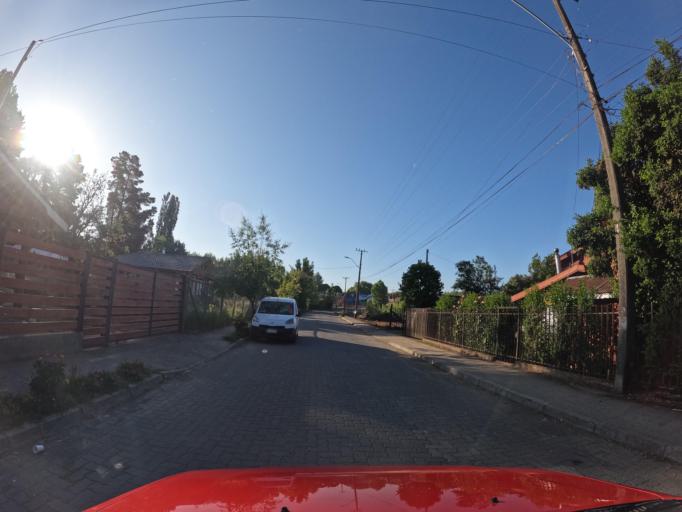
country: CL
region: Biobio
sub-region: Provincia de Concepcion
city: Lota
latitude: -37.1707
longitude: -72.9398
